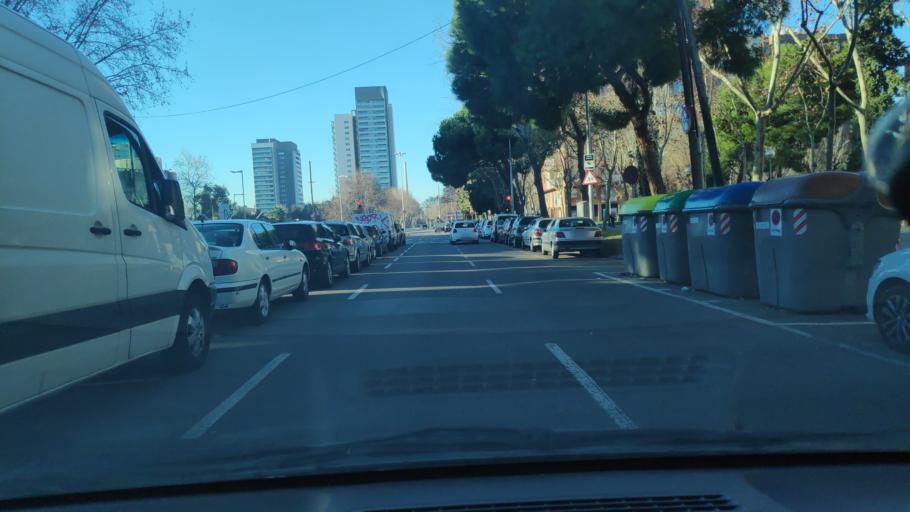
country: ES
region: Catalonia
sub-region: Provincia de Barcelona
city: Sant Marti
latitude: 41.4111
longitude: 2.2154
